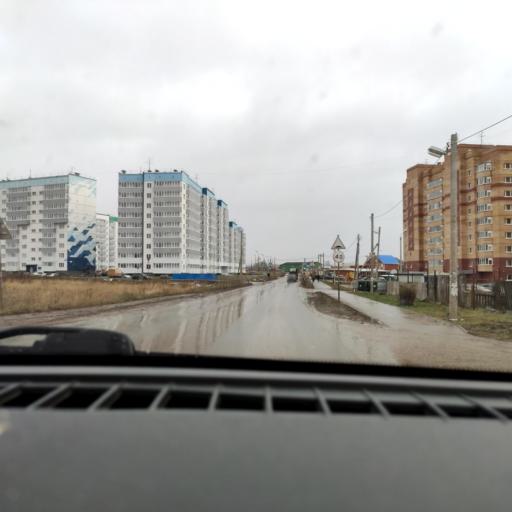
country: RU
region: Perm
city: Froly
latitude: 57.9219
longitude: 56.2760
